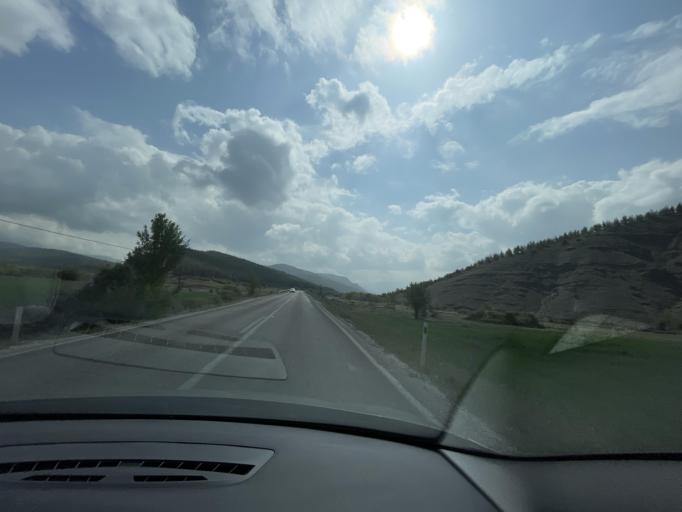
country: TR
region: Denizli
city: Acipayam
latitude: 37.5113
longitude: 29.4656
